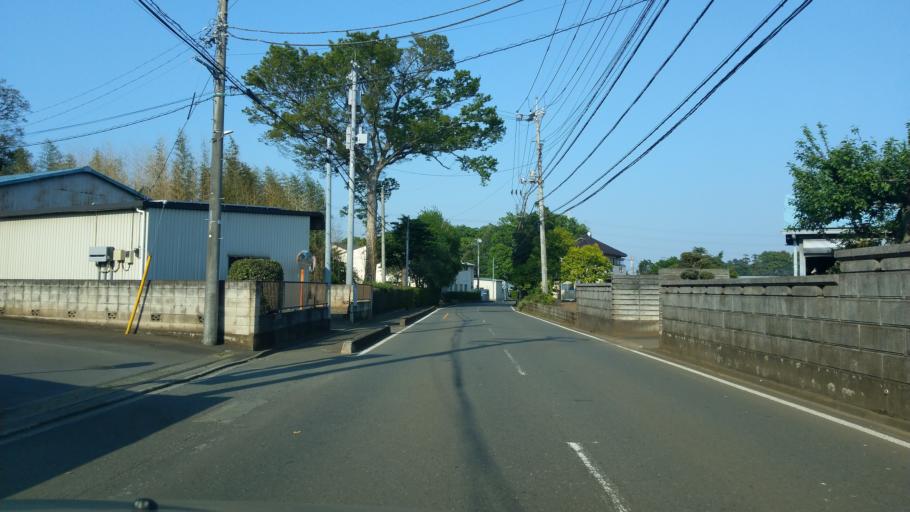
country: JP
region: Saitama
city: Oi
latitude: 35.8412
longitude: 139.4939
